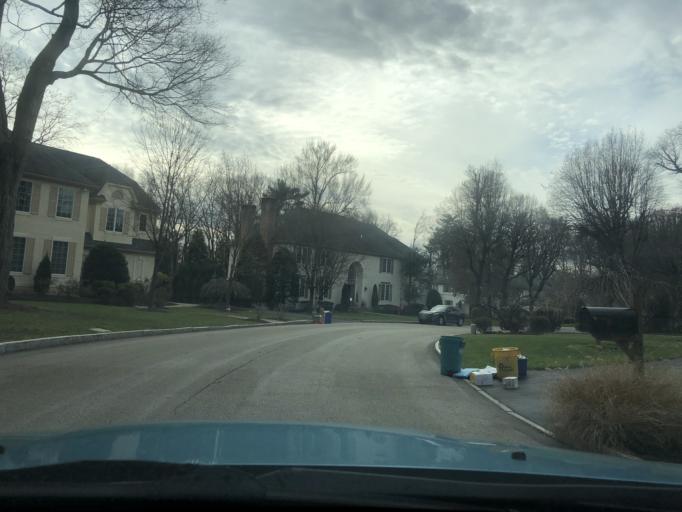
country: US
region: Pennsylvania
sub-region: Delaware County
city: Radnor
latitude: 40.0308
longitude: -75.3495
